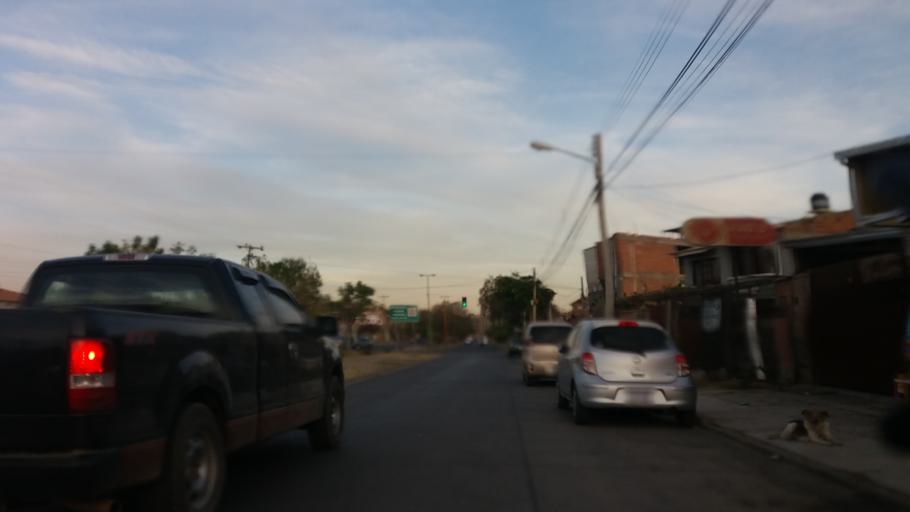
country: BO
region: Cochabamba
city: Cochabamba
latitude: -17.3790
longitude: -66.1889
